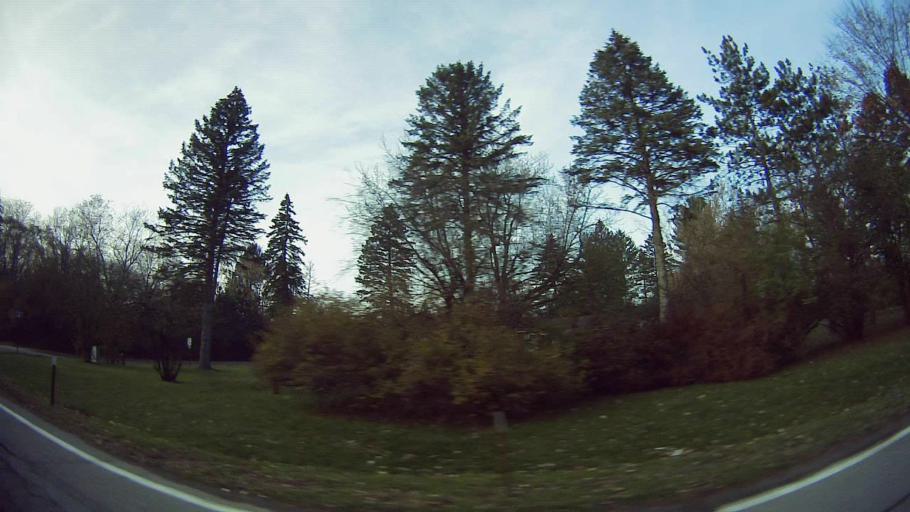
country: US
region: Michigan
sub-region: Oakland County
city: Bingham Farms
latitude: 42.5165
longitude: -83.2494
